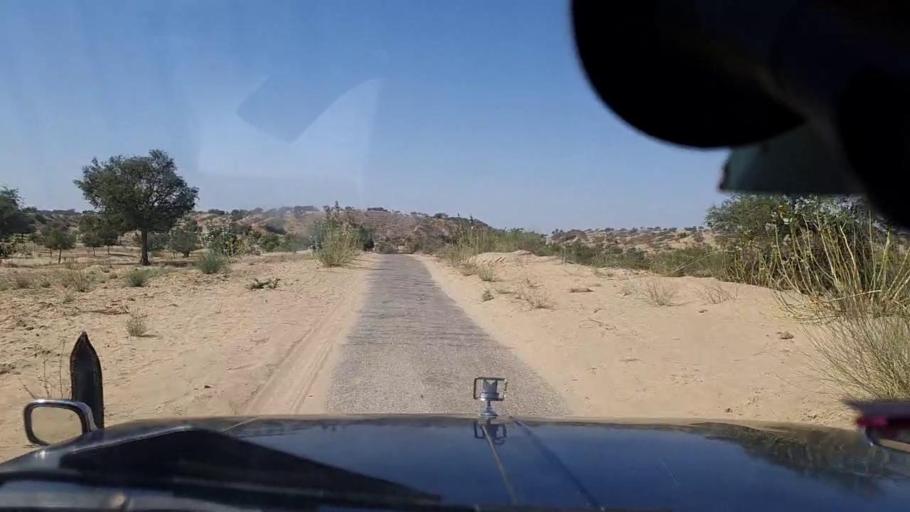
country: PK
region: Sindh
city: Mithi
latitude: 24.6126
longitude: 69.7187
